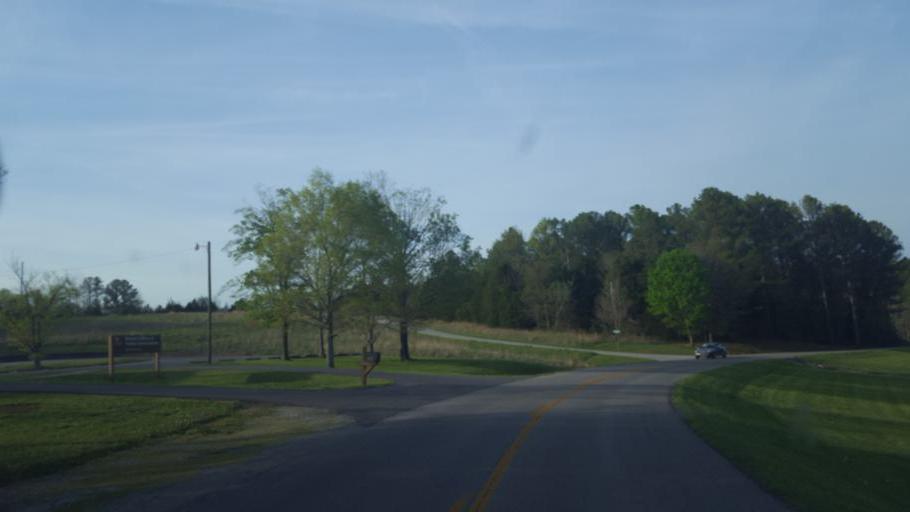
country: US
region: Kentucky
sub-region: Allen County
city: Scottsville
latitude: 36.8978
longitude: -86.1244
